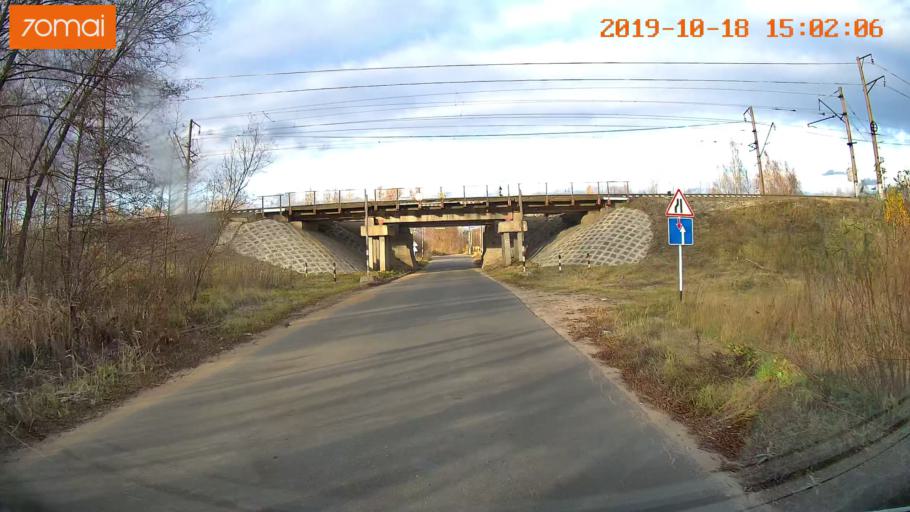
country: RU
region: Vladimir
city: Gus'-Khrustal'nyy
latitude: 55.5018
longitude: 40.6085
